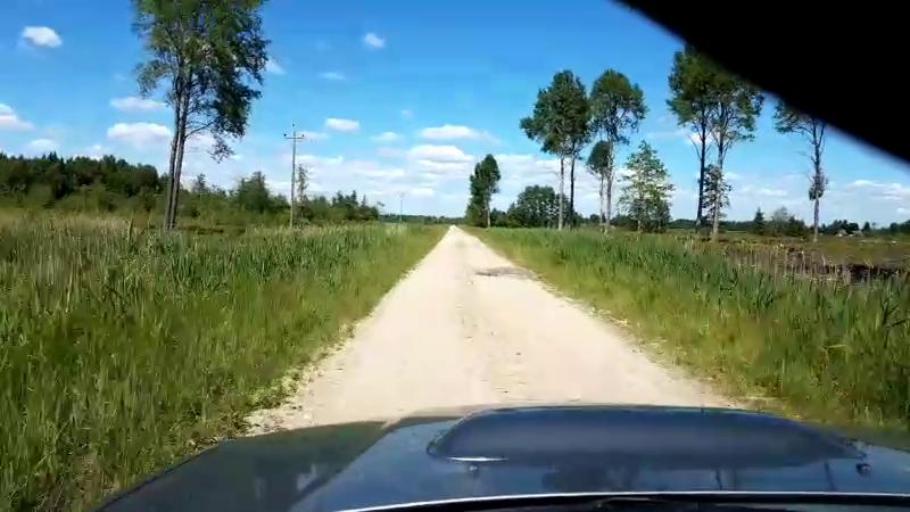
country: EE
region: Paernumaa
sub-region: Halinga vald
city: Parnu-Jaagupi
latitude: 58.5285
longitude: 24.5264
